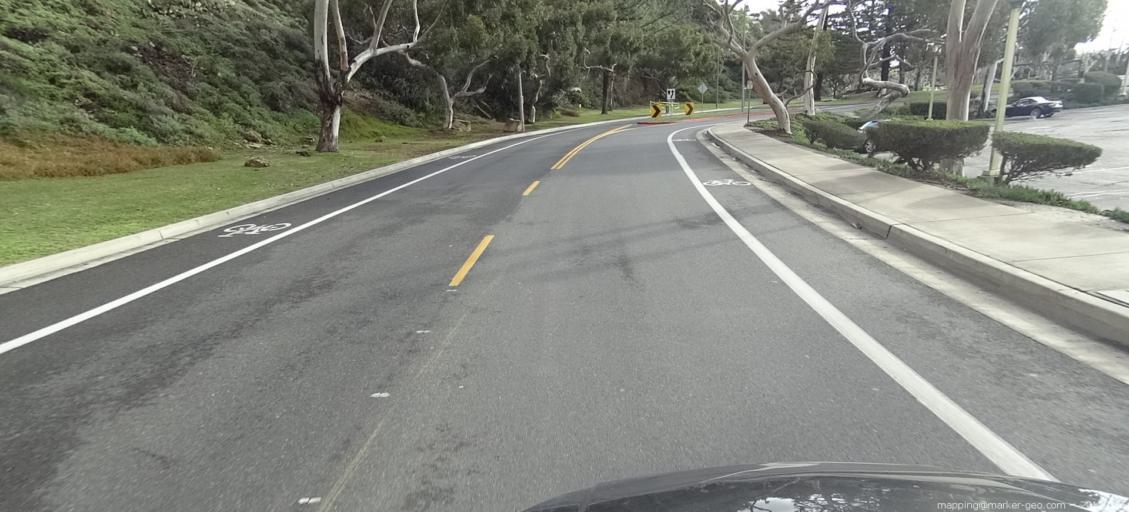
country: US
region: California
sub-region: Orange County
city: Dana Point
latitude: 33.4635
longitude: -117.7045
